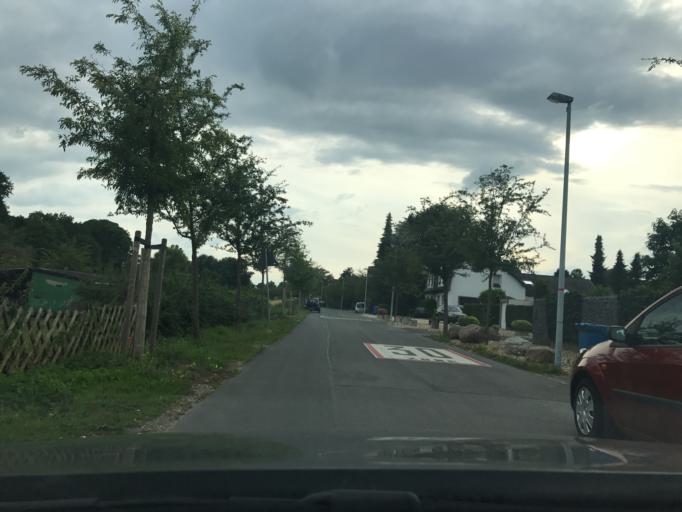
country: DE
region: North Rhine-Westphalia
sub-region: Regierungsbezirk Dusseldorf
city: Krefeld
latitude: 51.3631
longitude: 6.5957
